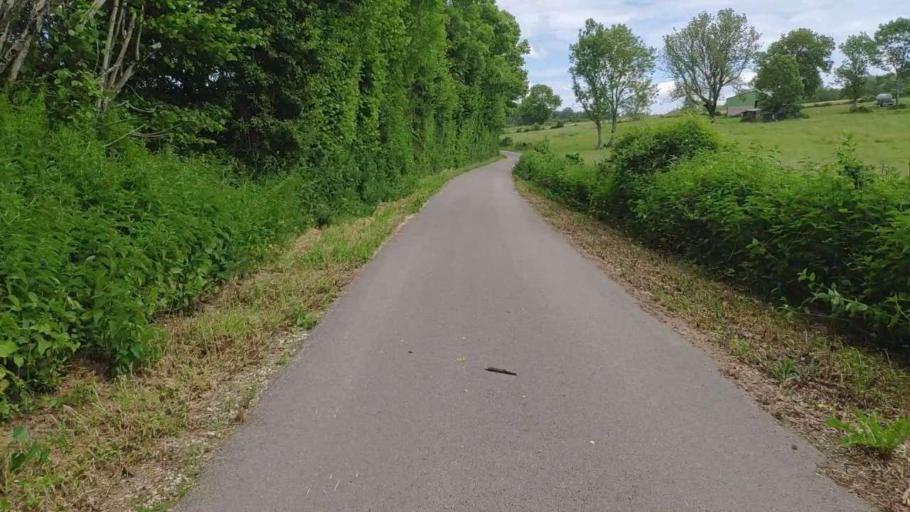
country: FR
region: Franche-Comte
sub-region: Departement du Jura
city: Poligny
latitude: 46.7652
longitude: 5.6545
